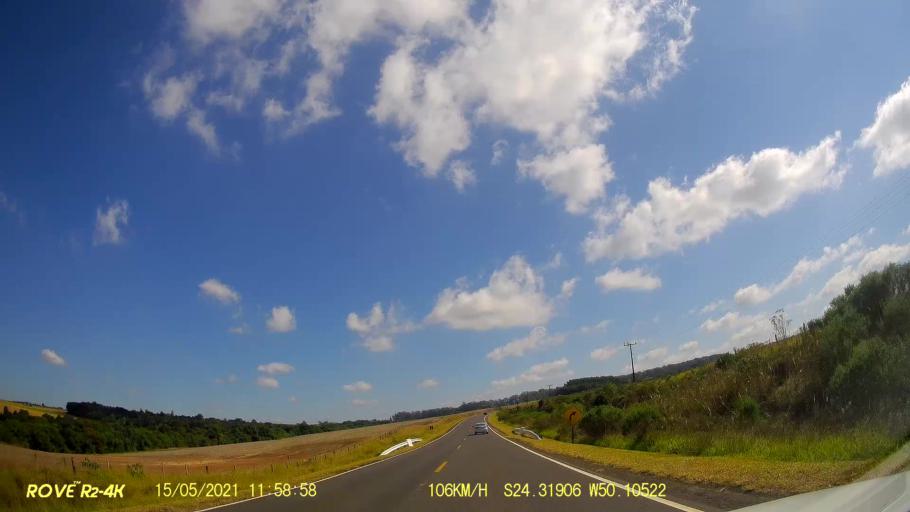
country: BR
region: Parana
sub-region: Pirai Do Sul
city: Pirai do Sul
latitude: -24.3189
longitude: -50.1048
